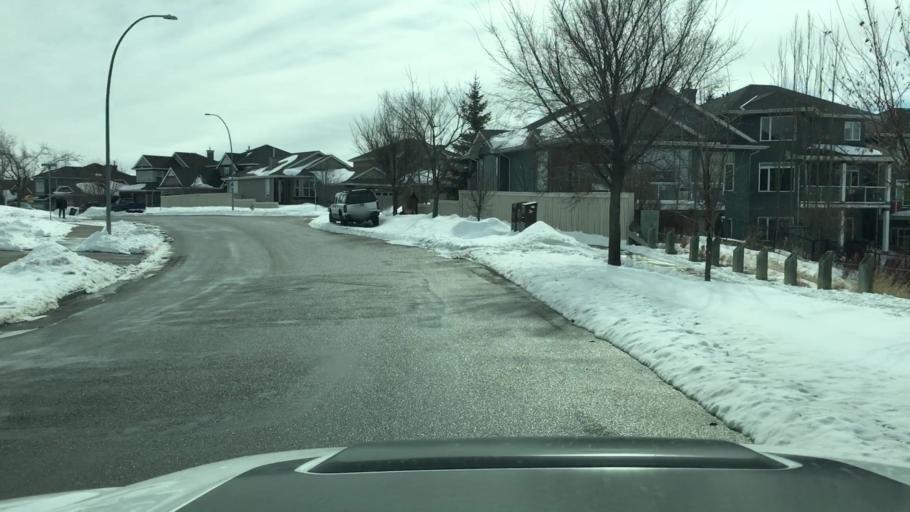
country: CA
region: Alberta
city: Calgary
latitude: 51.1481
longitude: -114.2320
